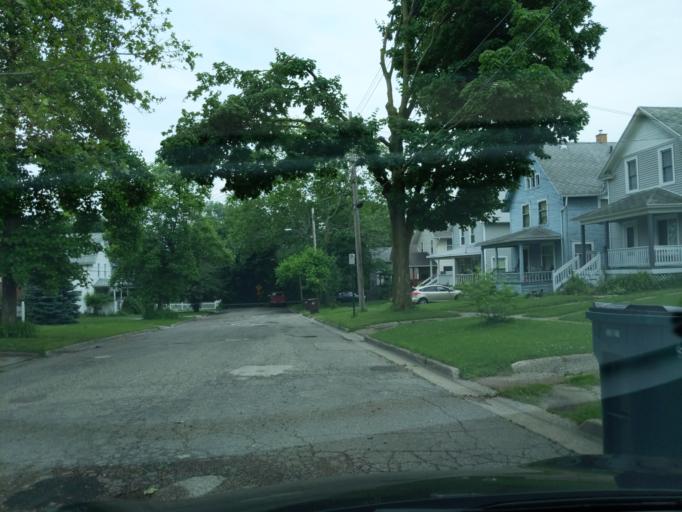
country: US
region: Michigan
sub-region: Ingham County
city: Lansing
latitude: 42.7448
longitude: -84.5514
